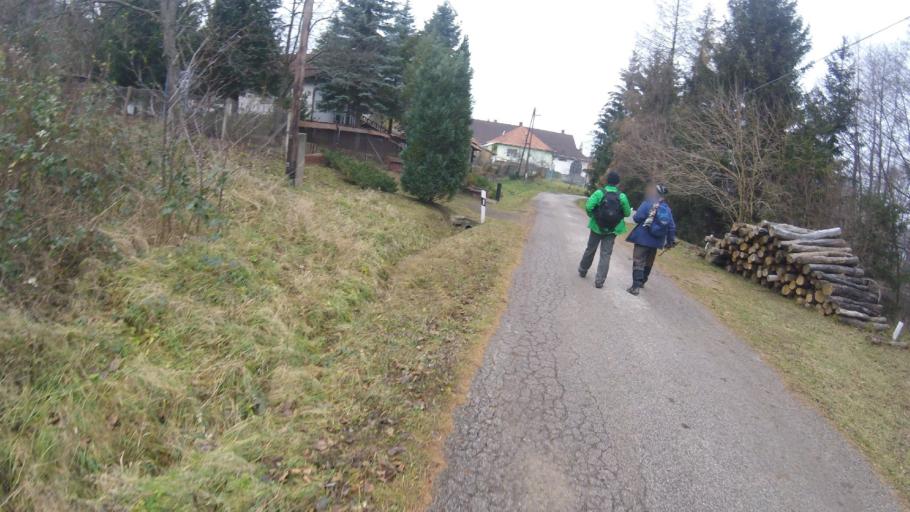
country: HU
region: Heves
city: Paradsasvar
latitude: 47.9323
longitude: 19.9162
